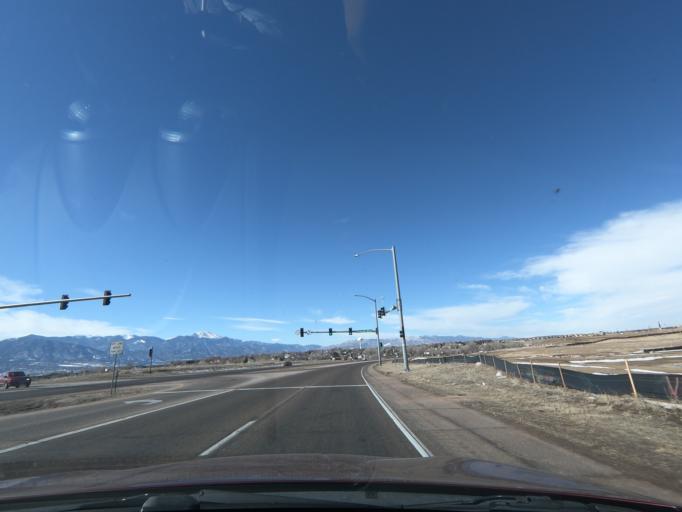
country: US
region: Colorado
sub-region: El Paso County
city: Security-Widefield
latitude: 38.7671
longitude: -104.7182
